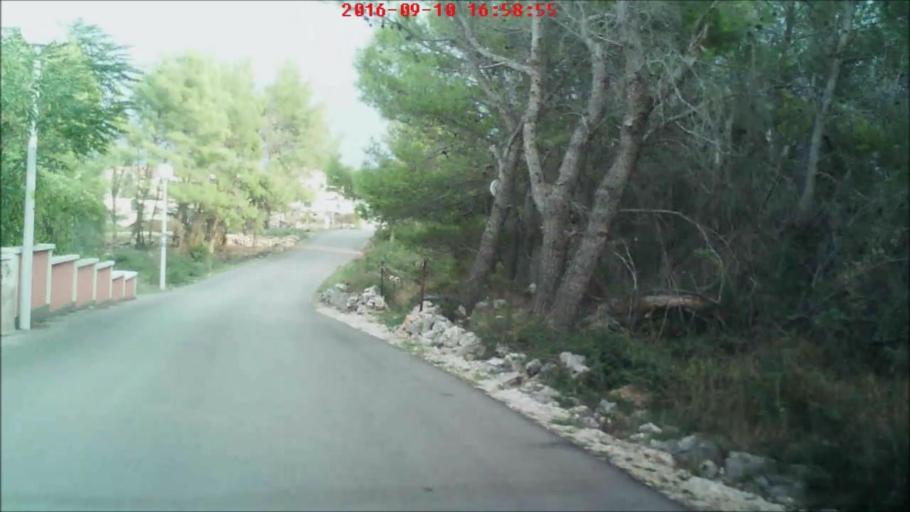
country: HR
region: Zadarska
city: Vir
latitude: 44.3138
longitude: 15.0516
